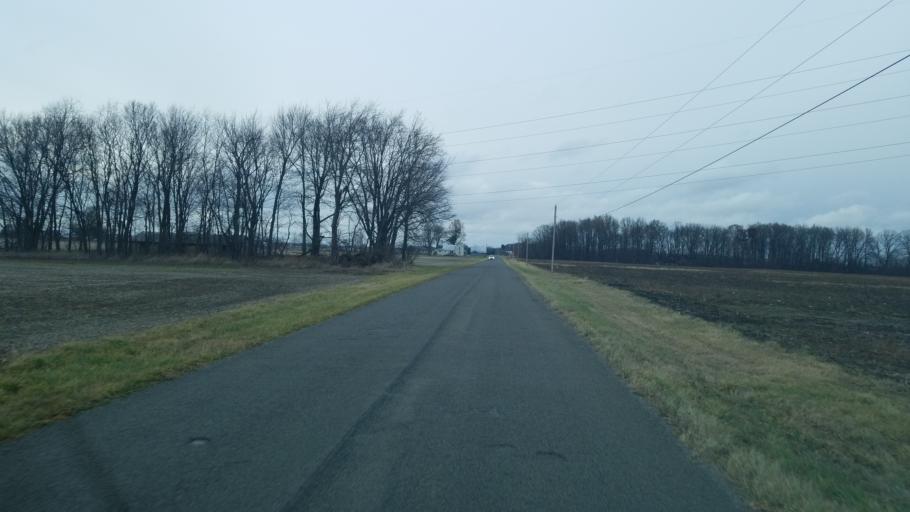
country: US
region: Ohio
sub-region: Union County
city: Richwood
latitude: 40.3081
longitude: -83.2518
